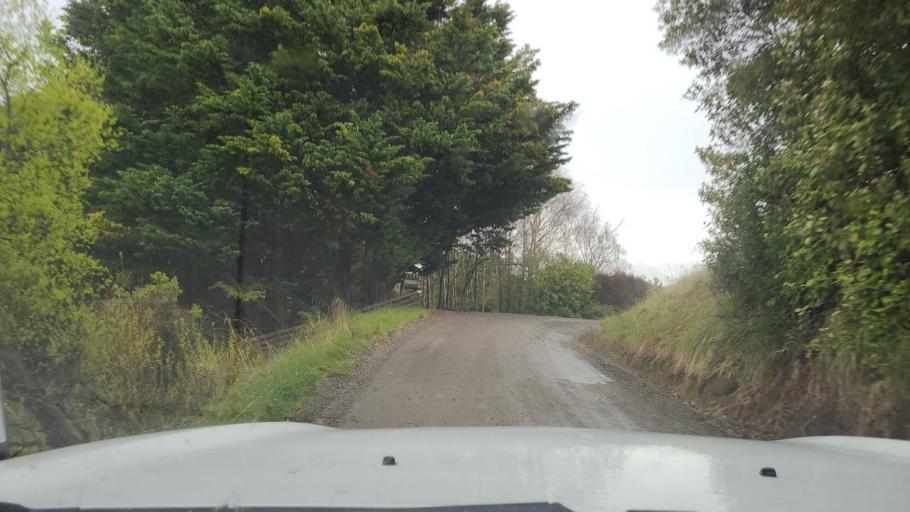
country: NZ
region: Wellington
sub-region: Masterton District
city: Masterton
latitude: -41.0850
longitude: 175.7251
